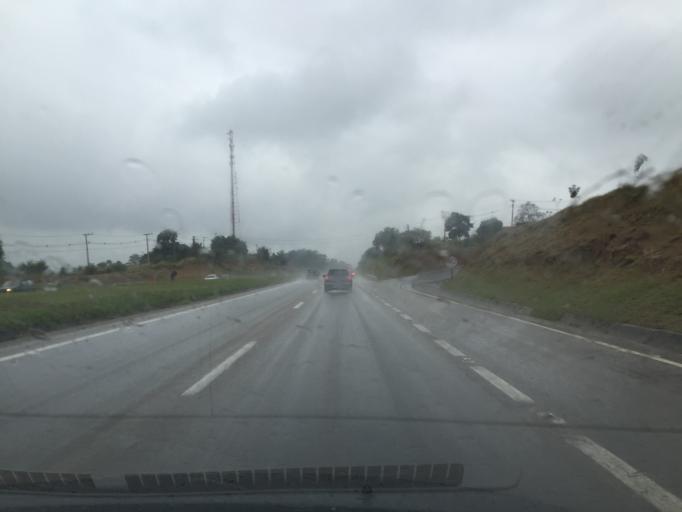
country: BR
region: Sao Paulo
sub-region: Itu
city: Itu
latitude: -23.3758
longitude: -47.3274
